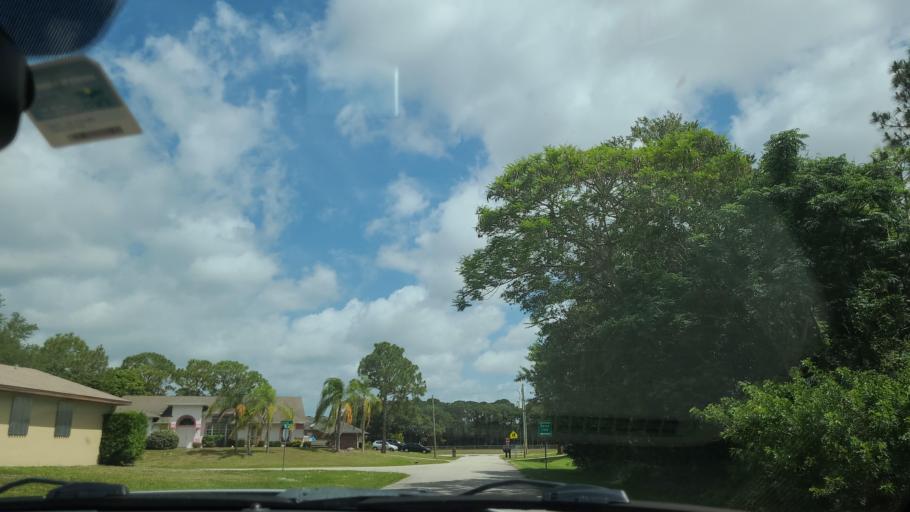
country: US
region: Florida
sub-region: Brevard County
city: West Melbourne
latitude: 28.0234
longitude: -80.6571
